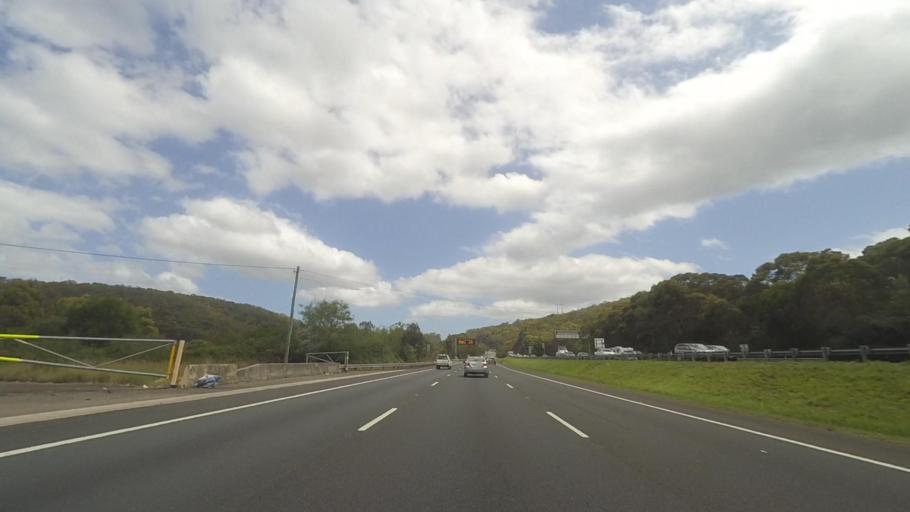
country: AU
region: New South Wales
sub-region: Hornsby Shire
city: Berowra
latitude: -33.5584
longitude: 151.1928
